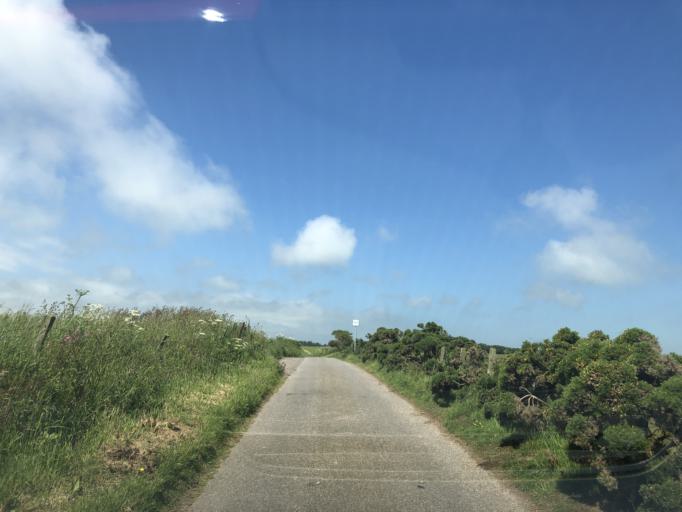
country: GB
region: Scotland
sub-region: Aberdeenshire
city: Stonehaven
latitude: 56.9132
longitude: -2.2018
